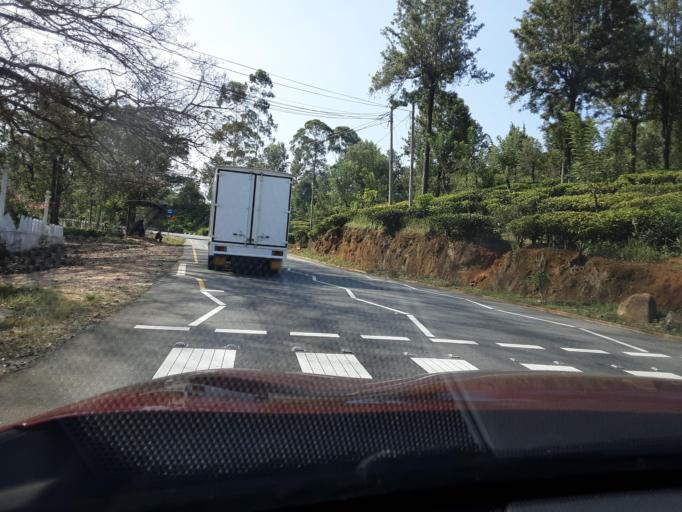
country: LK
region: Uva
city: Badulla
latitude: 6.9584
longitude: 81.1174
